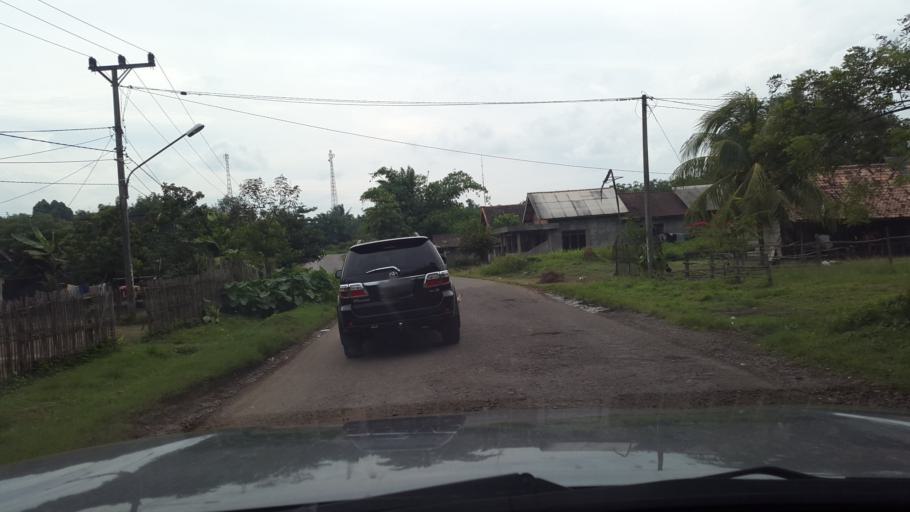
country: ID
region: South Sumatra
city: Gunungmenang
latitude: -3.3343
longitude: 104.0037
